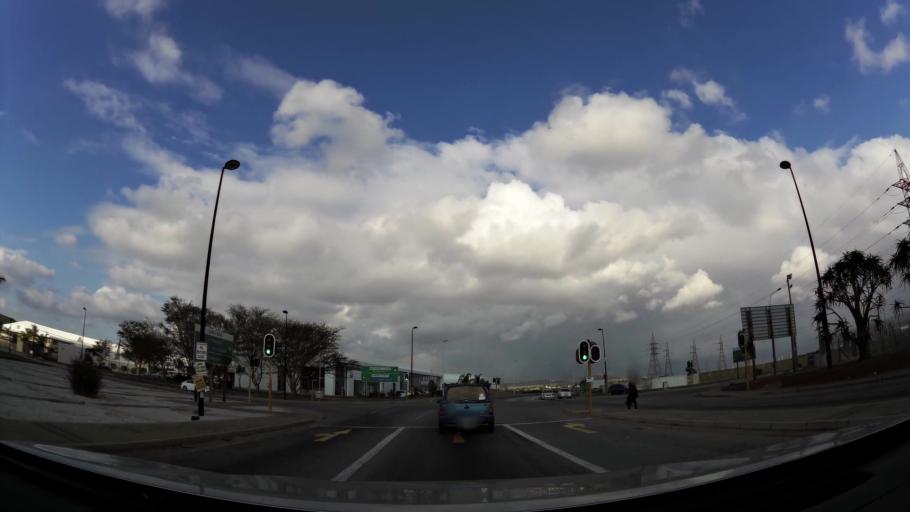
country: ZA
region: Eastern Cape
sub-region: Nelson Mandela Bay Metropolitan Municipality
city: Uitenhage
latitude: -33.7861
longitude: 25.4243
